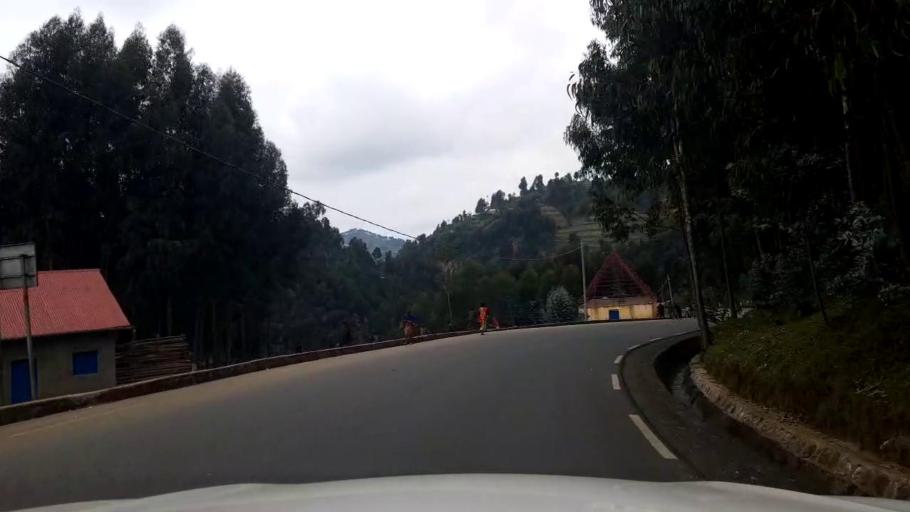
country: RW
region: Northern Province
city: Musanze
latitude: -1.6479
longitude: 29.5067
